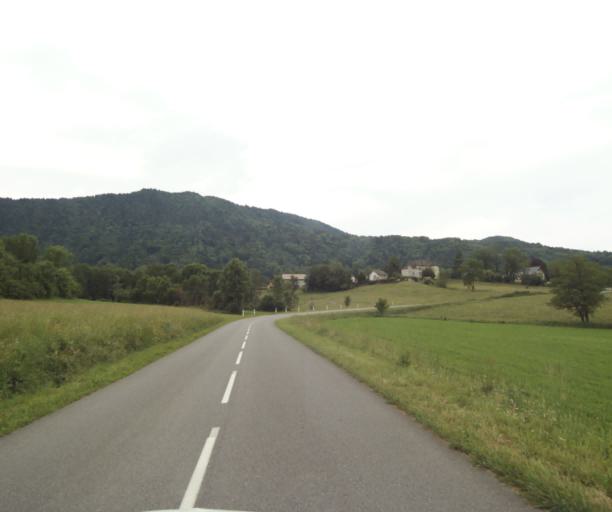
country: FR
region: Rhone-Alpes
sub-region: Departement de la Haute-Savoie
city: Allinges
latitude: 46.3139
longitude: 6.4794
